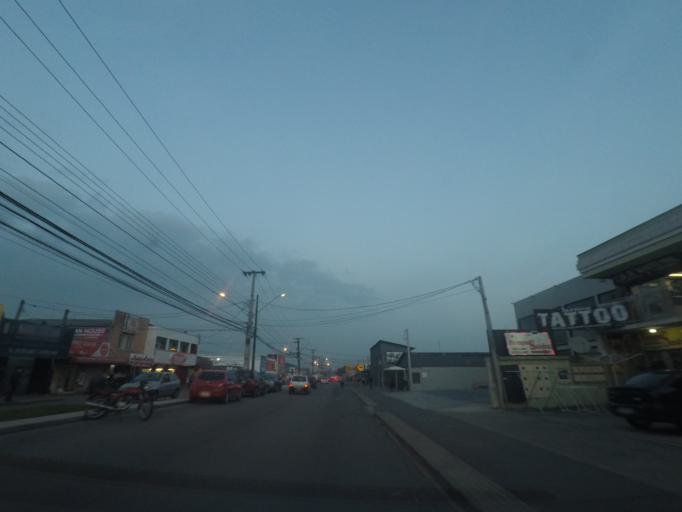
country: BR
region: Parana
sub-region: Pinhais
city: Pinhais
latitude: -25.4511
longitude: -49.1791
